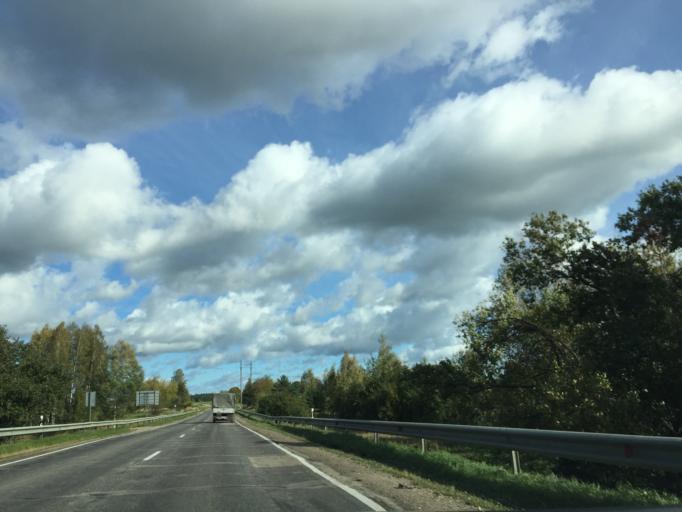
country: LV
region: Rezekne
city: Rezekne
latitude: 56.5426
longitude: 27.3036
